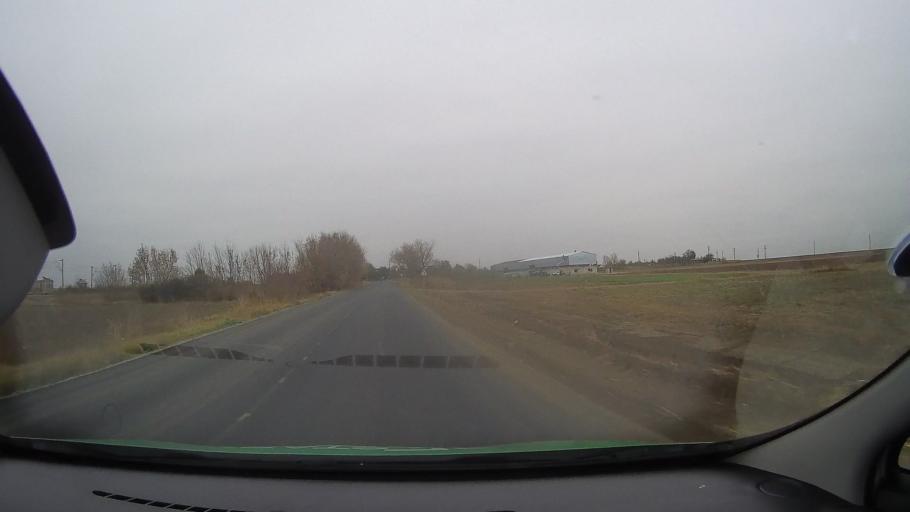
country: RO
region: Ialomita
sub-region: Comuna Valea Ciorii
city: Valea Ciorii
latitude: 44.7389
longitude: 27.5776
